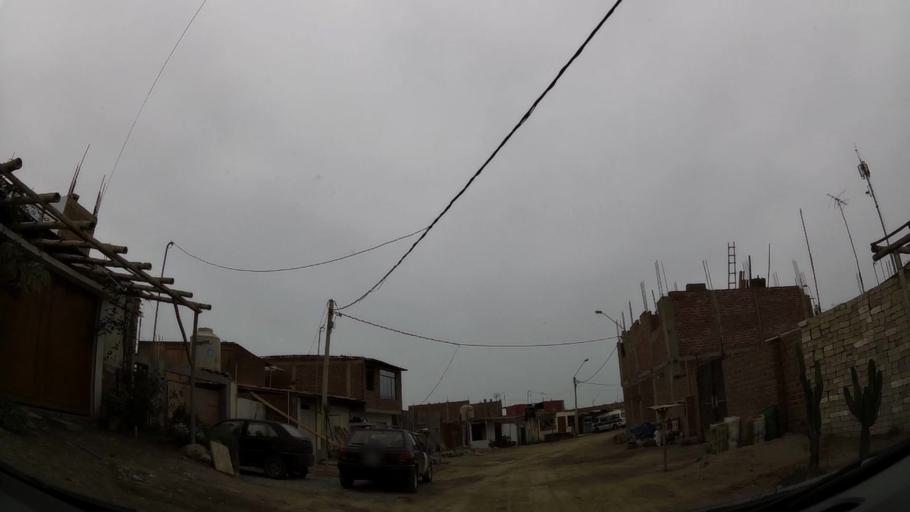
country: PE
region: Lima
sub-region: Lima
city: Punta Hermosa
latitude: -12.3191
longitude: -76.8333
